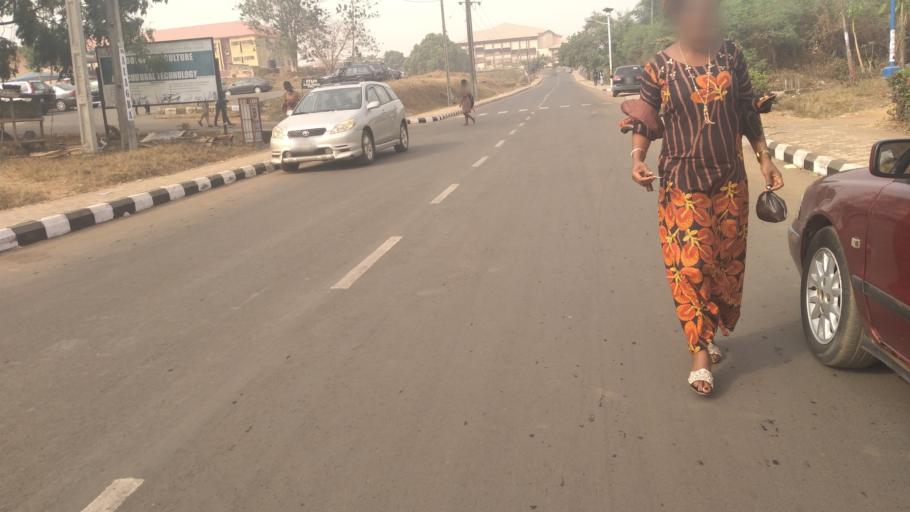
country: NG
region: Ondo
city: Ilare
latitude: 7.3010
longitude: 5.1361
